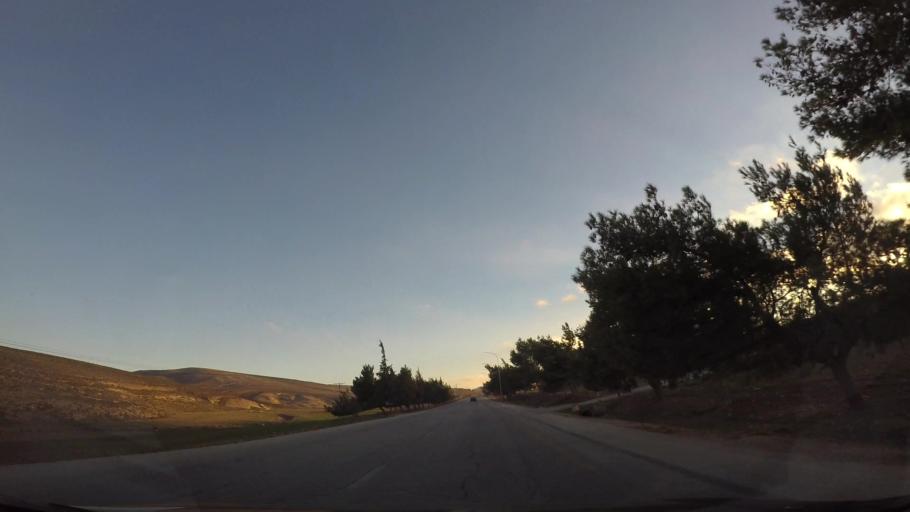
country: JO
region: Ma'an
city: Petra
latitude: 30.4487
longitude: 35.5244
